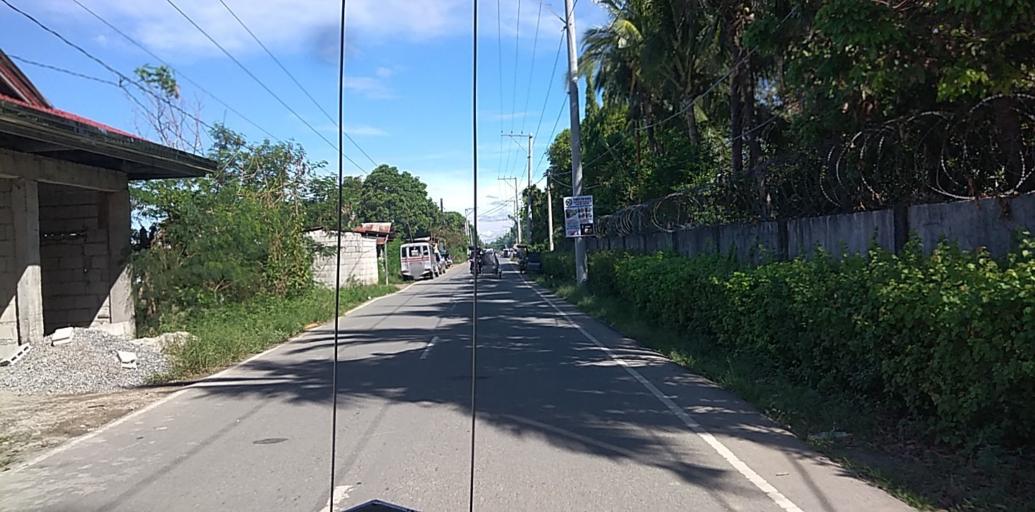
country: PH
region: Central Luzon
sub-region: Province of Pampanga
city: Candaba
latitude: 15.0907
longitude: 120.8116
